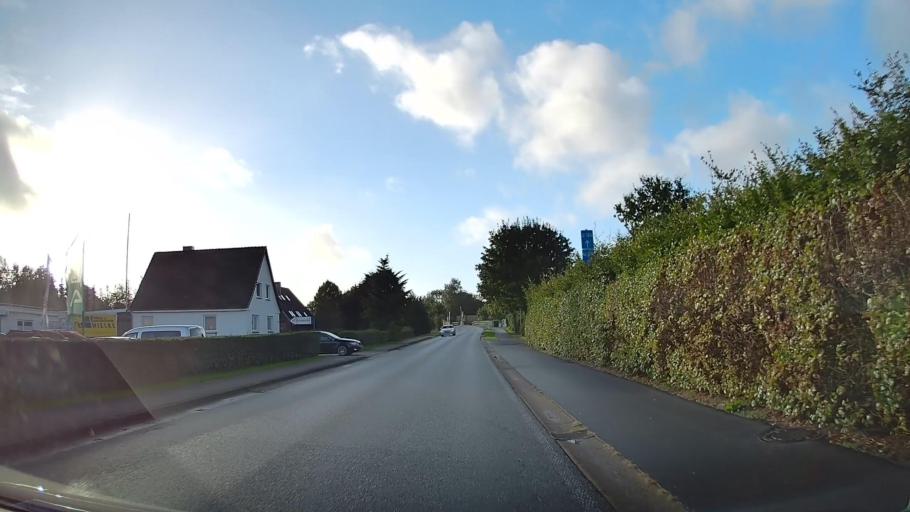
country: DE
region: Schleswig-Holstein
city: Horst
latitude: 53.8050
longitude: 9.6470
